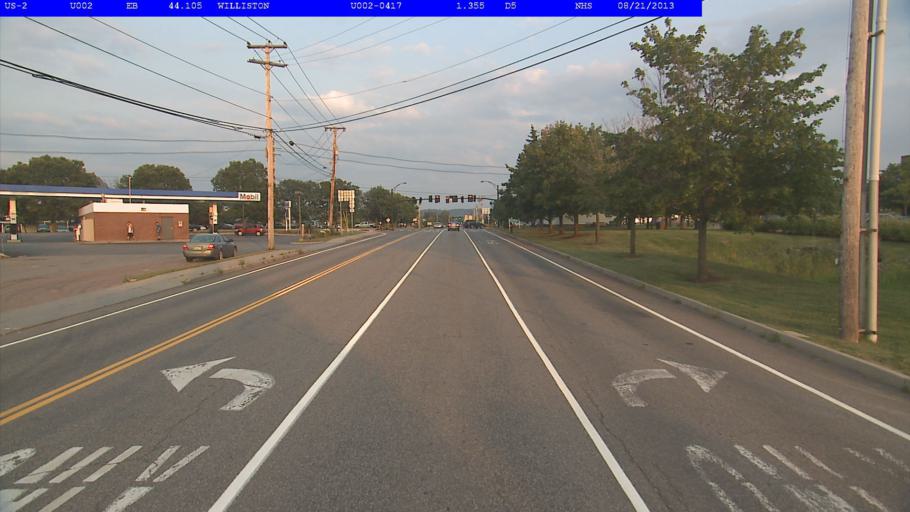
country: US
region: Vermont
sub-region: Chittenden County
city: Essex Junction
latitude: 44.4501
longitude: -73.1123
